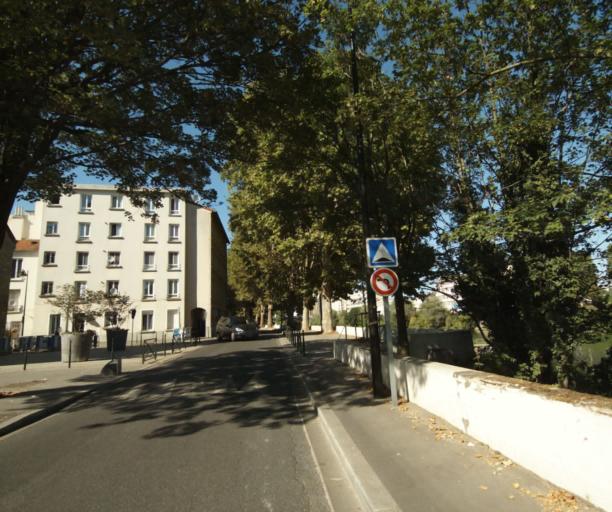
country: FR
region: Ile-de-France
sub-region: Departement de Seine-Saint-Denis
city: Villetaneuse
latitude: 48.9327
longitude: 2.3406
